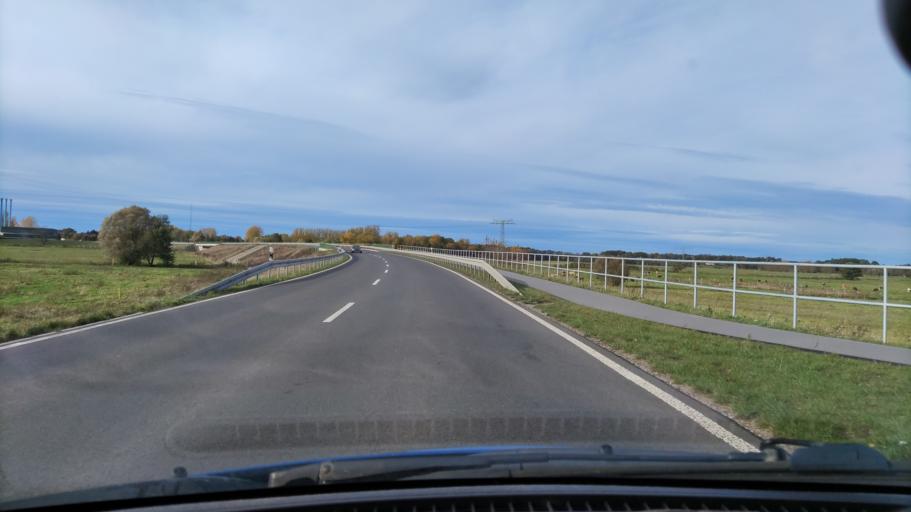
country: DE
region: Brandenburg
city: Breese
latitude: 53.0073
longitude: 11.7767
